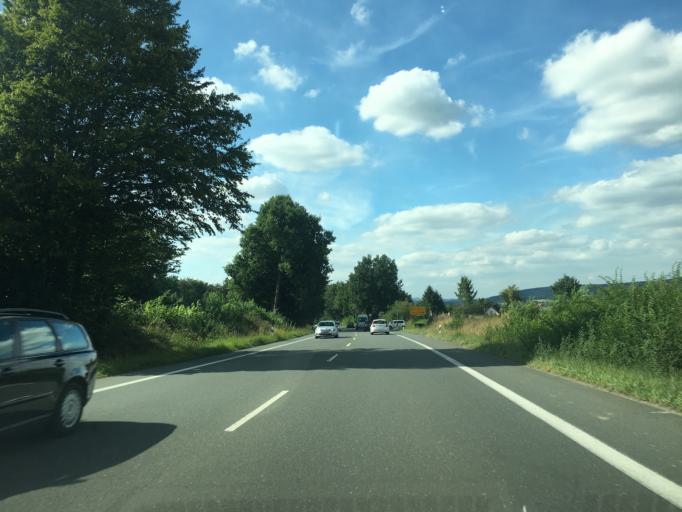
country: DE
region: North Rhine-Westphalia
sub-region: Regierungsbezirk Detmold
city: Dorentrup
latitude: 52.0030
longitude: 8.9689
